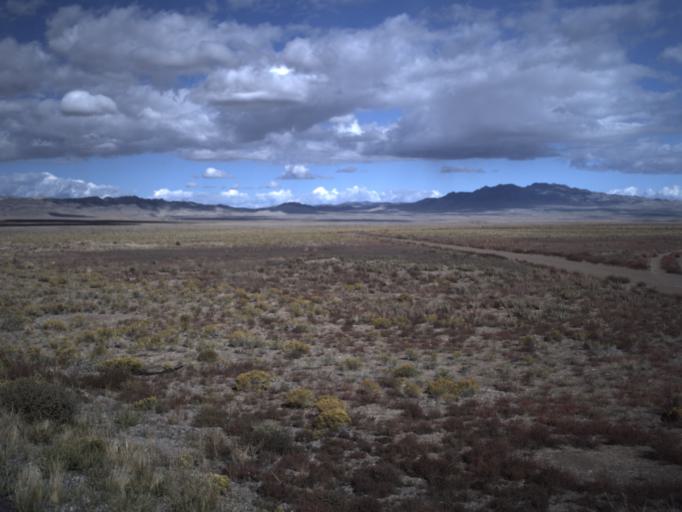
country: US
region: Utah
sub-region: Beaver County
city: Milford
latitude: 38.5358
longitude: -113.6912
